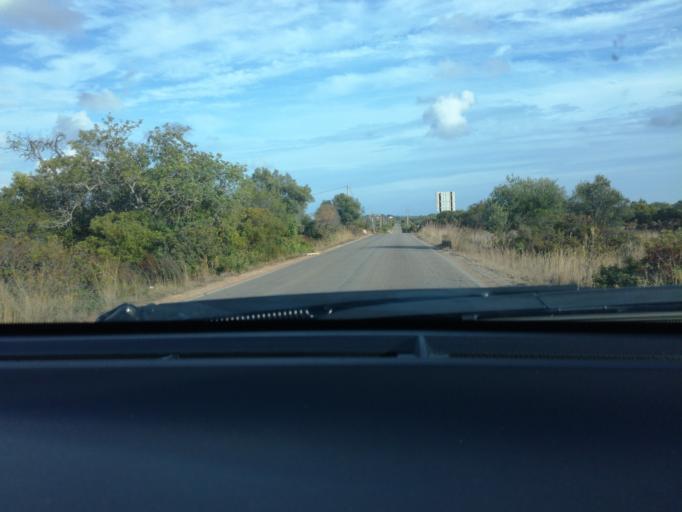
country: PT
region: Faro
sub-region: Olhao
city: Laranjeiro
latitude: 37.0807
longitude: -7.8348
